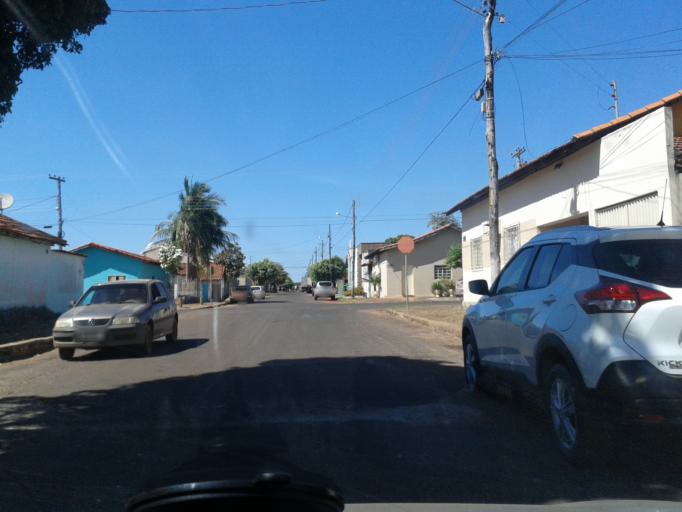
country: BR
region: Goias
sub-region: Sao Miguel Do Araguaia
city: Sao Miguel do Araguaia
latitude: -13.2753
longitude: -50.1596
